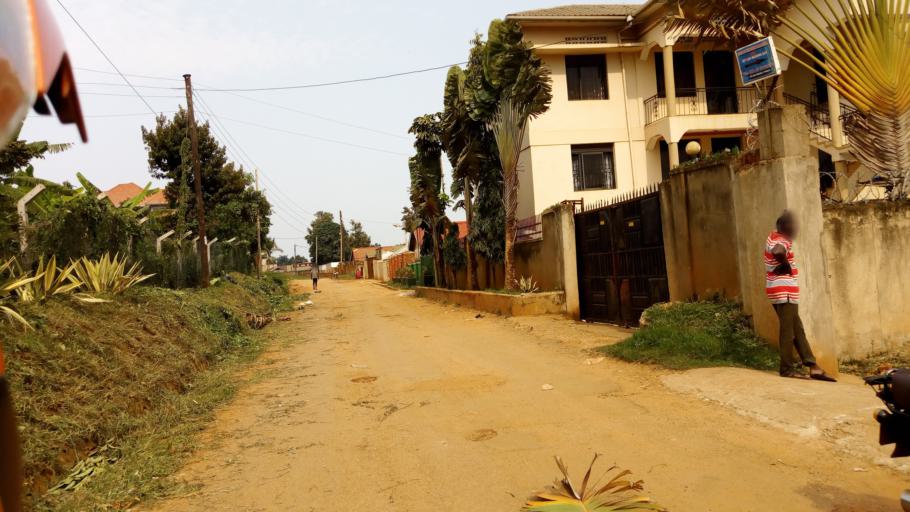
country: UG
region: Central Region
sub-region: Wakiso District
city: Kireka
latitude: 0.3117
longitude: 32.6418
